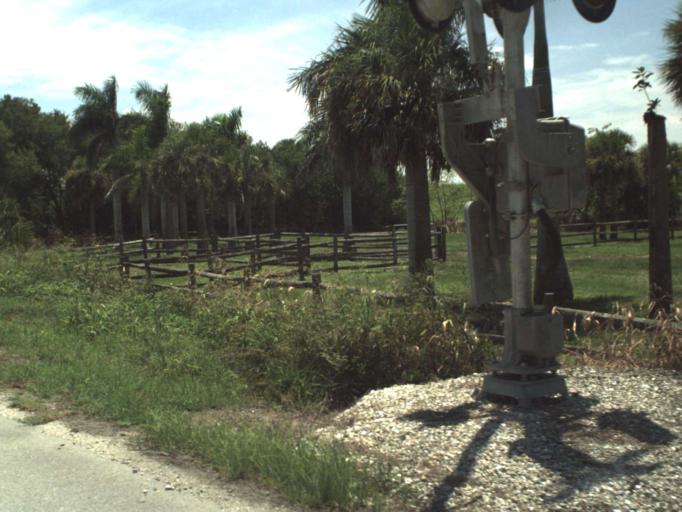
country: US
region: Florida
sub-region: Palm Beach County
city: Pahokee
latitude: 26.9495
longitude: -80.6096
